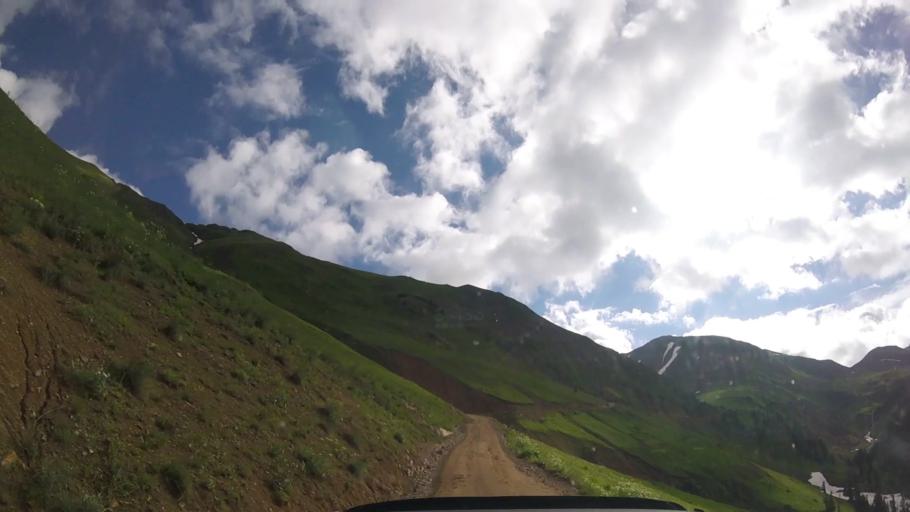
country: US
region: Colorado
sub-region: San Juan County
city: Silverton
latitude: 37.9126
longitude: -107.6421
